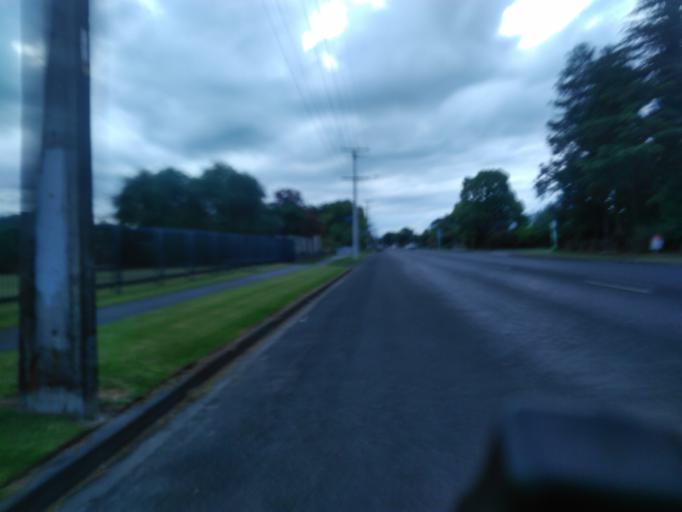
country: NZ
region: Gisborne
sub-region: Gisborne District
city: Gisborne
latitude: -38.6447
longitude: 178.0067
